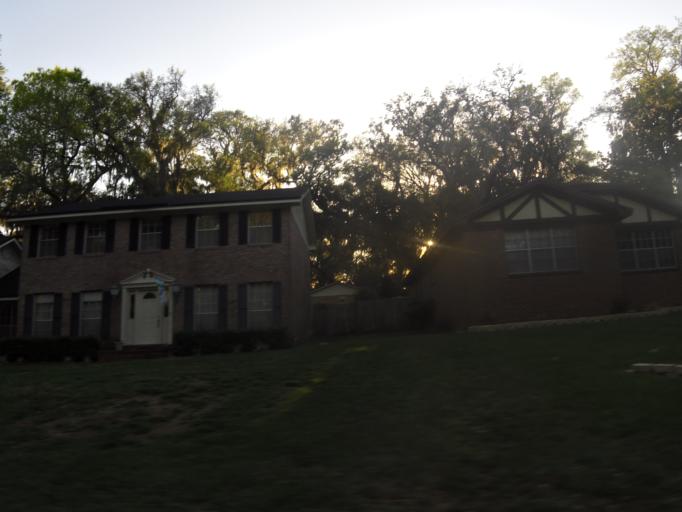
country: US
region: Florida
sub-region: Duval County
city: Atlantic Beach
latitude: 30.3830
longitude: -81.5044
